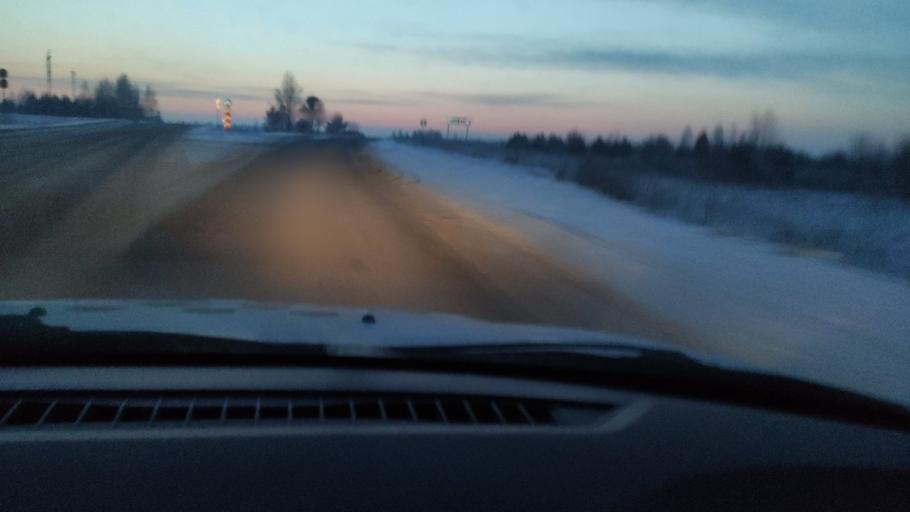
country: RU
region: Perm
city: Kungur
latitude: 57.4066
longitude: 56.8971
